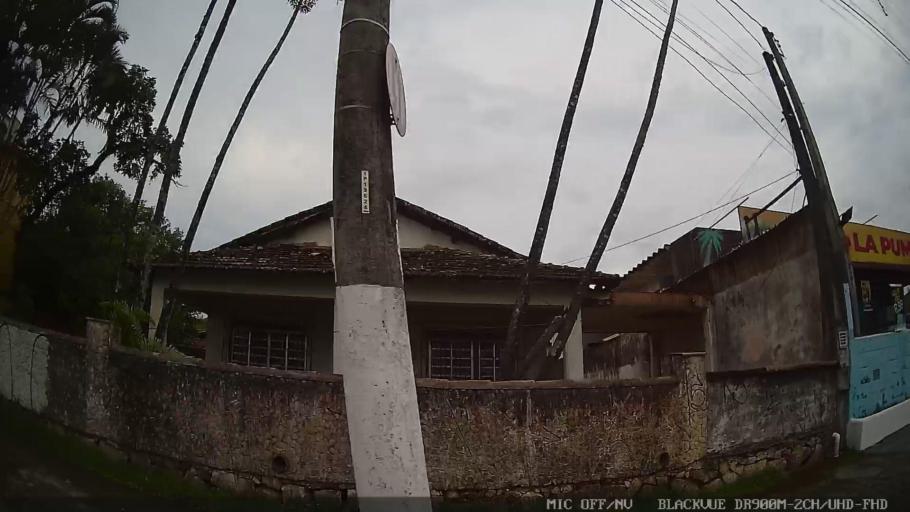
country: BR
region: Sao Paulo
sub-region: Caraguatatuba
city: Caraguatatuba
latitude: -23.6247
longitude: -45.3796
